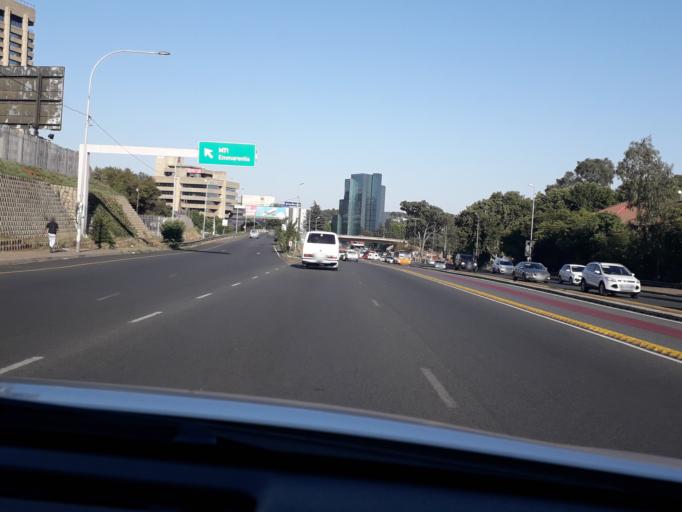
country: ZA
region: Gauteng
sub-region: City of Johannesburg Metropolitan Municipality
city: Johannesburg
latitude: -26.1841
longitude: 28.0233
